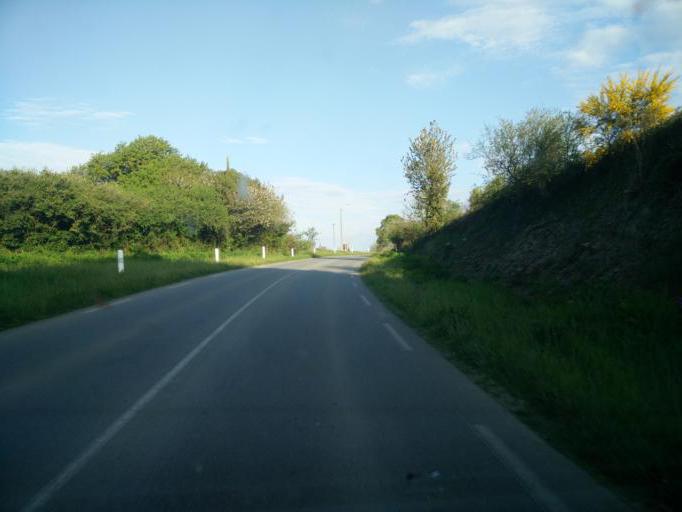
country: FR
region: Brittany
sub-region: Departement des Cotes-d'Armor
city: Plurien
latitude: 48.6187
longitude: -2.4322
